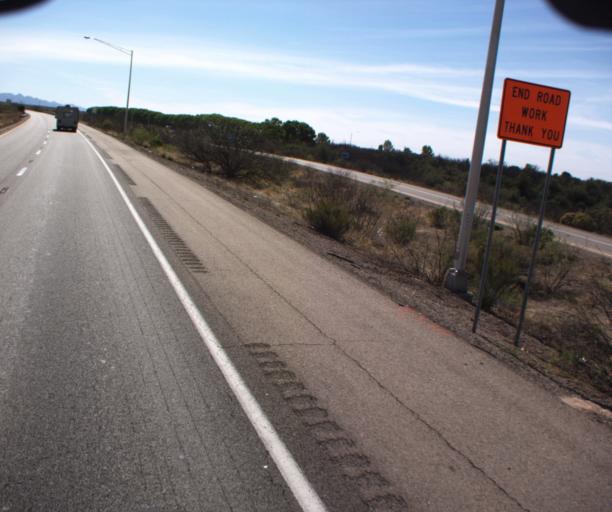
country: US
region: Arizona
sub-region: Cochise County
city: Benson
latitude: 31.9673
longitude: -110.2766
